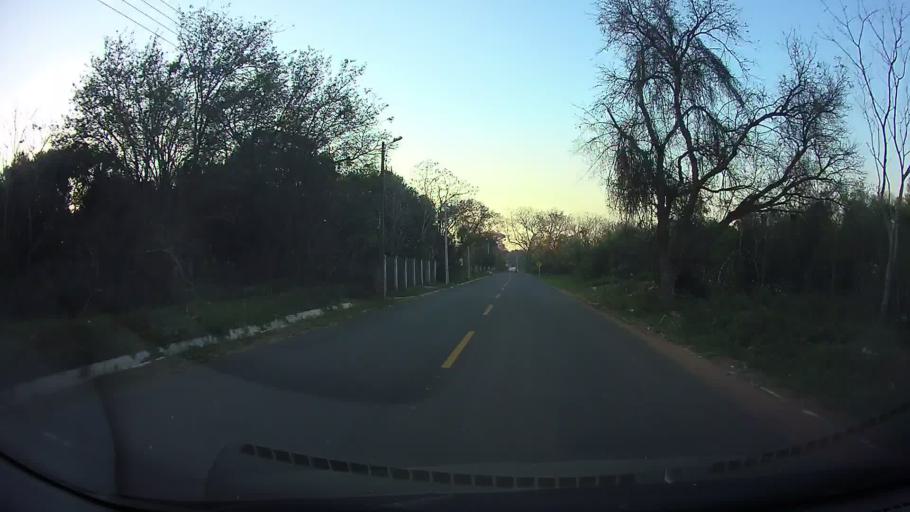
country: PY
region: Central
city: Limpio
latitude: -25.2419
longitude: -57.4947
